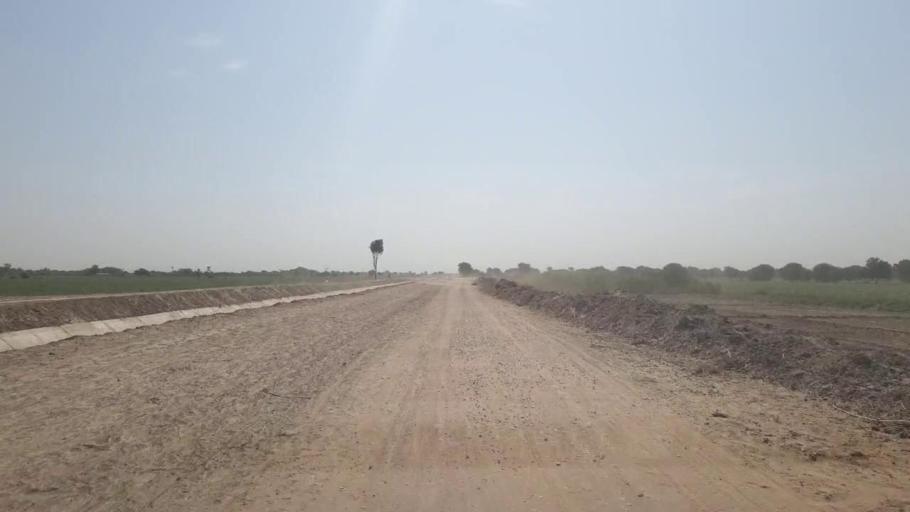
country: PK
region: Sindh
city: Kunri
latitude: 25.2696
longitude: 69.6269
